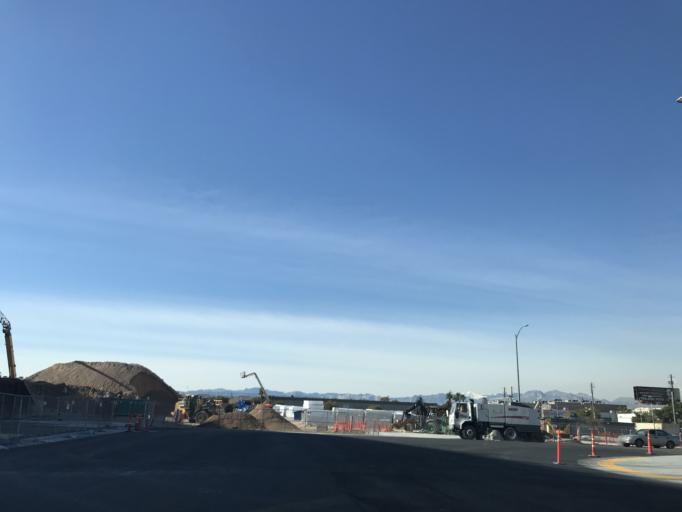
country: US
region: Nevada
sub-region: Clark County
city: Paradise
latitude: 36.0926
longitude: -115.1829
